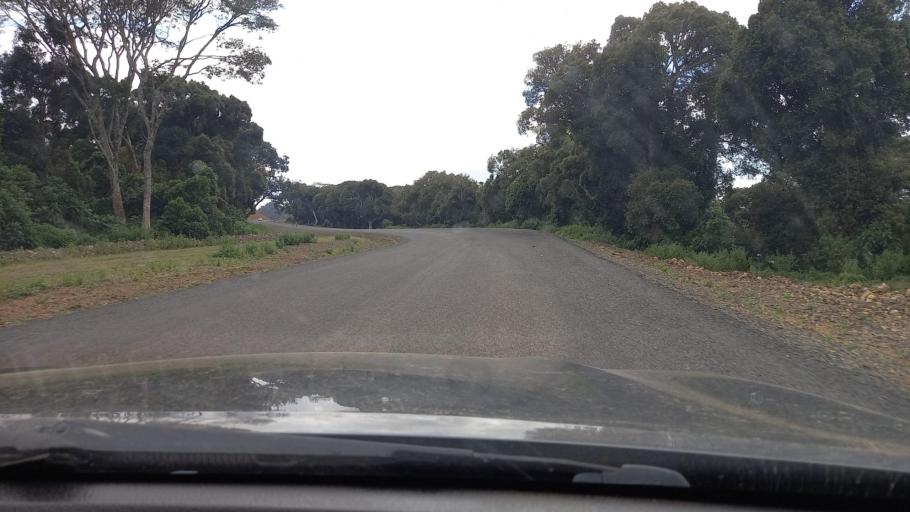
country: ET
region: Southern Nations, Nationalities, and People's Region
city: Mizan Teferi
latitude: 6.2081
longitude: 35.6088
